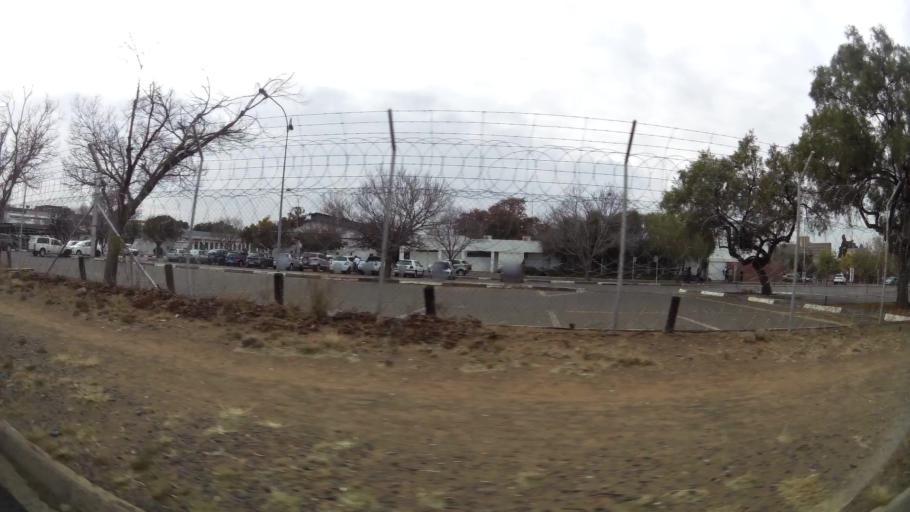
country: ZA
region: Orange Free State
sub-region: Mangaung Metropolitan Municipality
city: Bloemfontein
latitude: -29.1128
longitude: 26.1832
